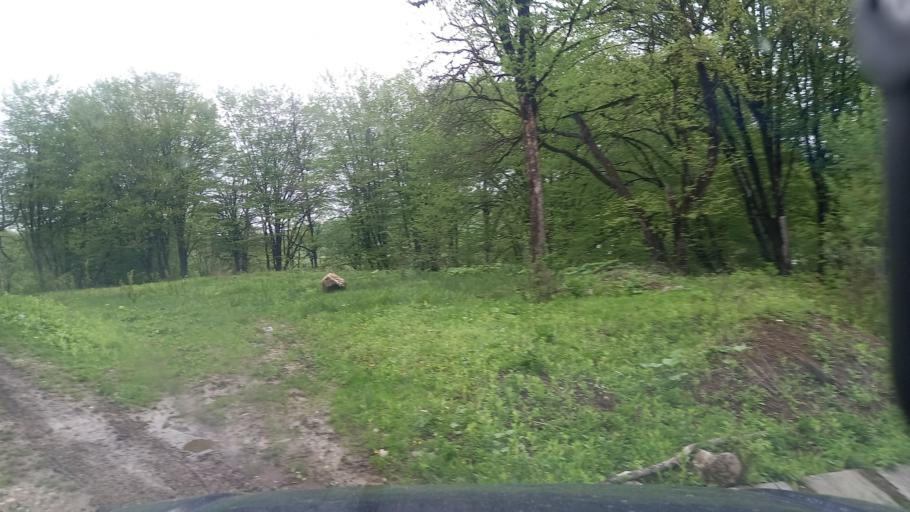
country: RU
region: Kabardino-Balkariya
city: Babugent
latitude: 43.2266
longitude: 43.5597
